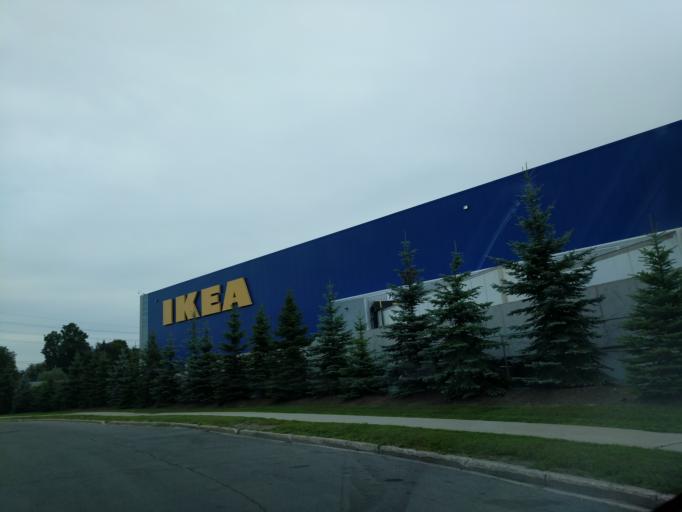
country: CA
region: Ontario
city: Bells Corners
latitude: 45.3509
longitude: -75.7827
